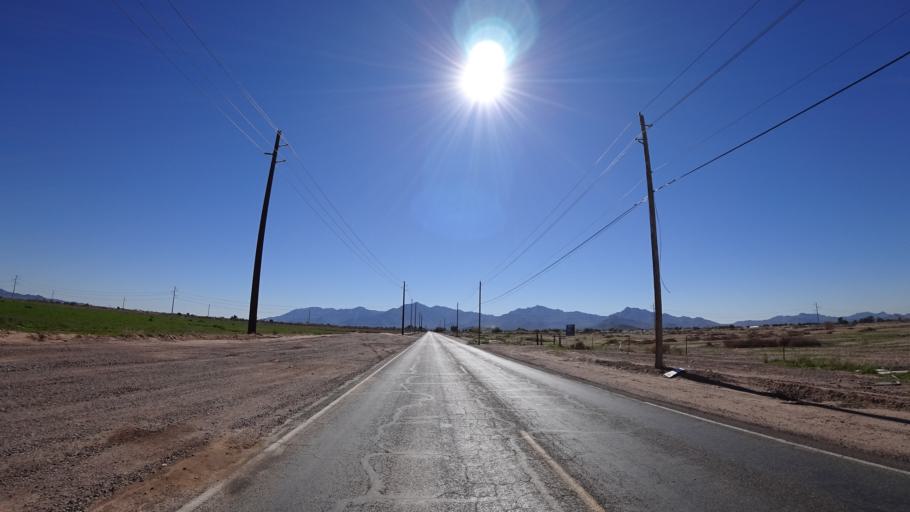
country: US
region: Arizona
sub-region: Maricopa County
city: Tolleson
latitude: 33.4037
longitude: -112.2892
